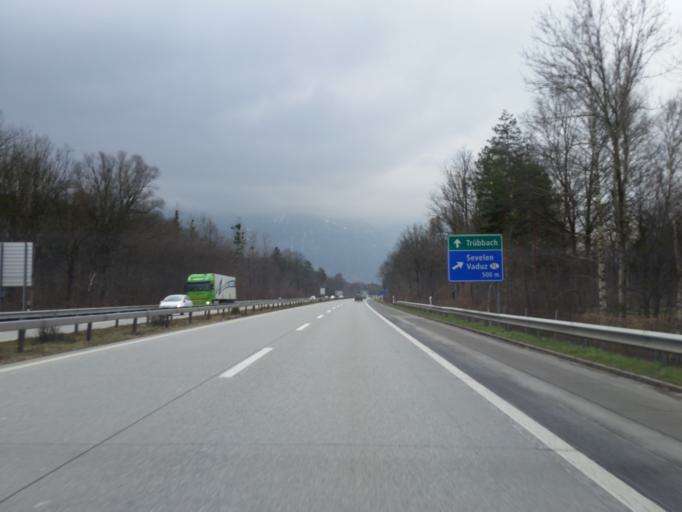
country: LI
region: Vaduz
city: Vaduz
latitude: 47.1406
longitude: 9.5045
